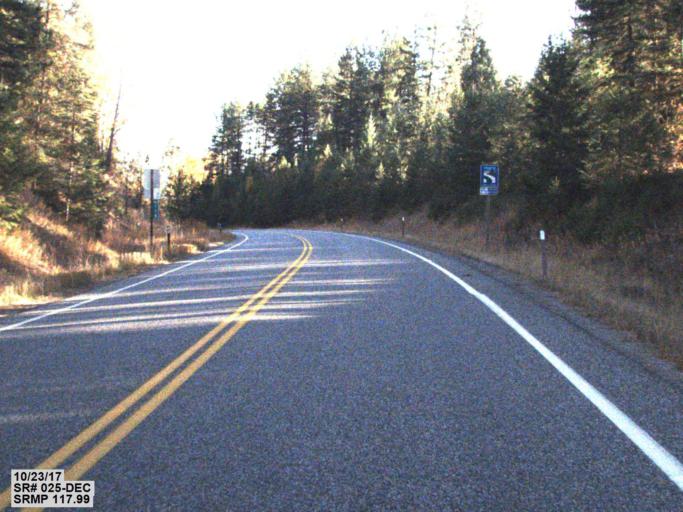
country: CA
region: British Columbia
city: Rossland
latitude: 48.9596
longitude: -117.8027
